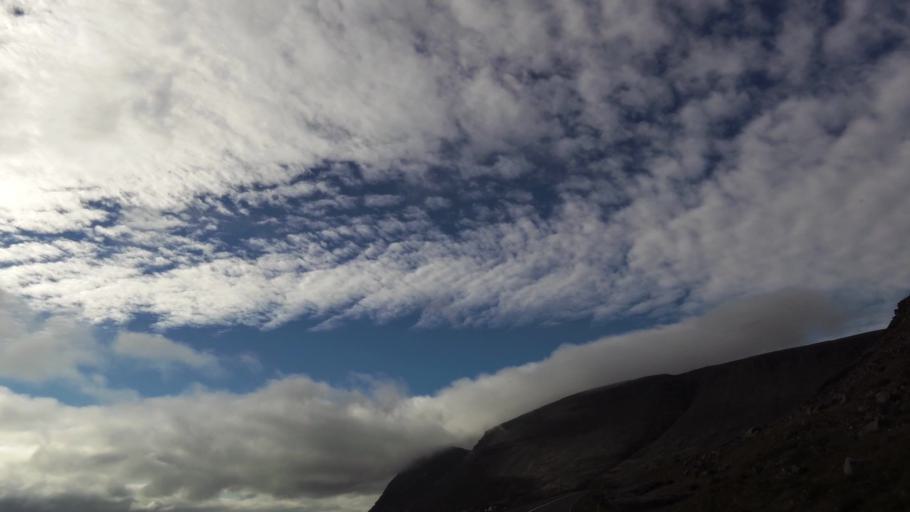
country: IS
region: West
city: Olafsvik
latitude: 65.5848
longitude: -23.9679
